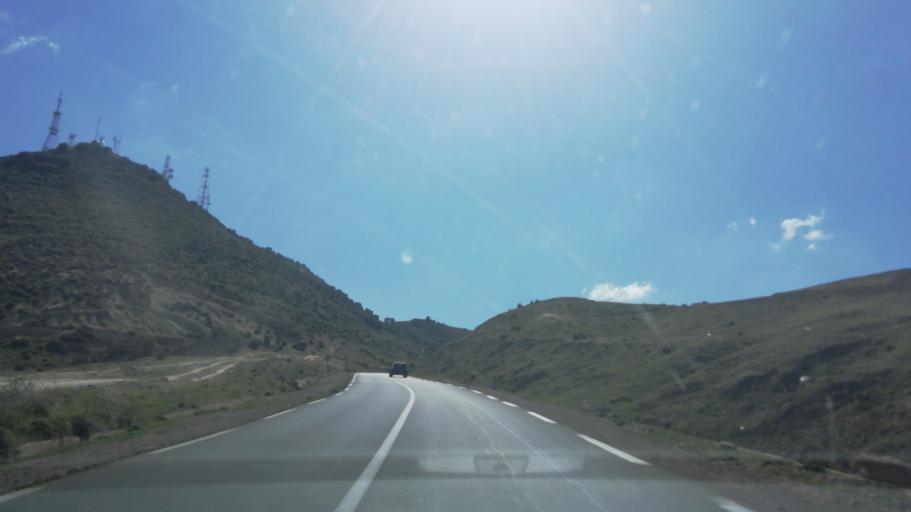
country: DZ
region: Mascara
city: Mascara
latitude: 35.4787
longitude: 0.1587
